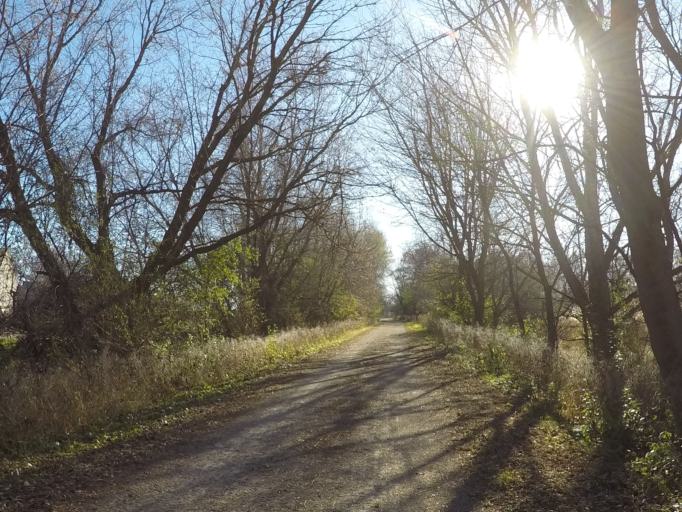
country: US
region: Wisconsin
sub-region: Dane County
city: Deerfield
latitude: 43.0448
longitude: -89.0519
